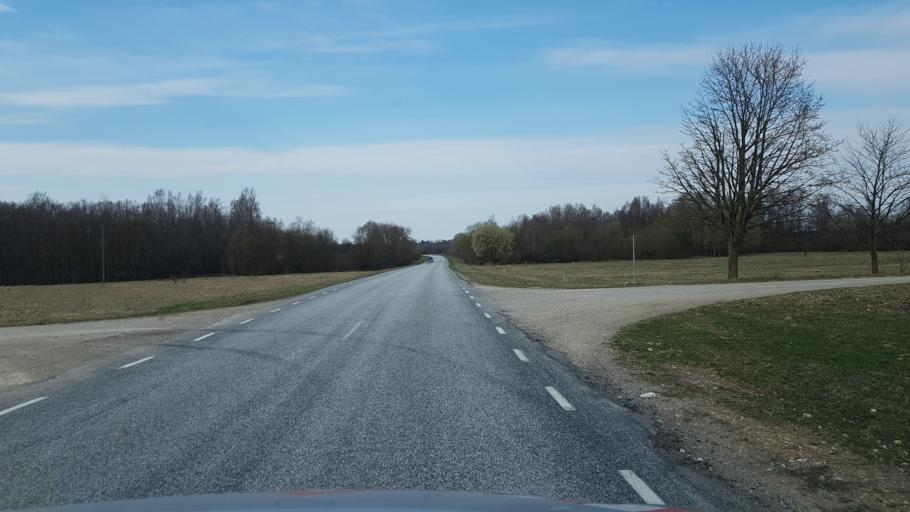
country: EE
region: Laeaene-Virumaa
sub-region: Haljala vald
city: Haljala
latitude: 59.4802
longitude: 26.1557
